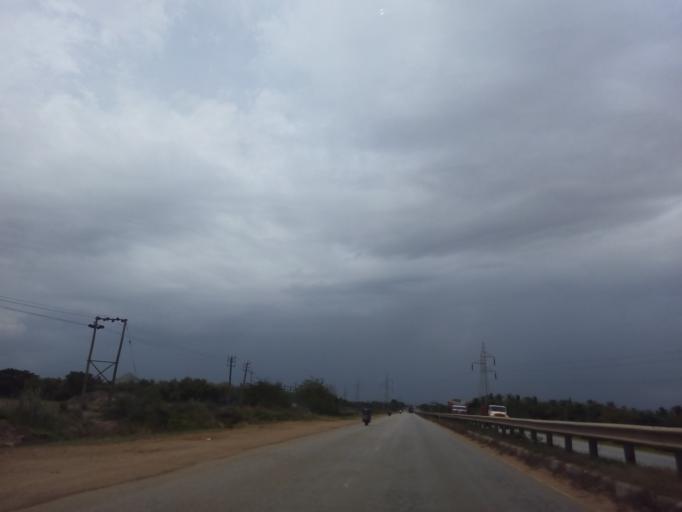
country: IN
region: Karnataka
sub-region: Davanagere
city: Harihar
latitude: 14.4824
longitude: 75.8064
